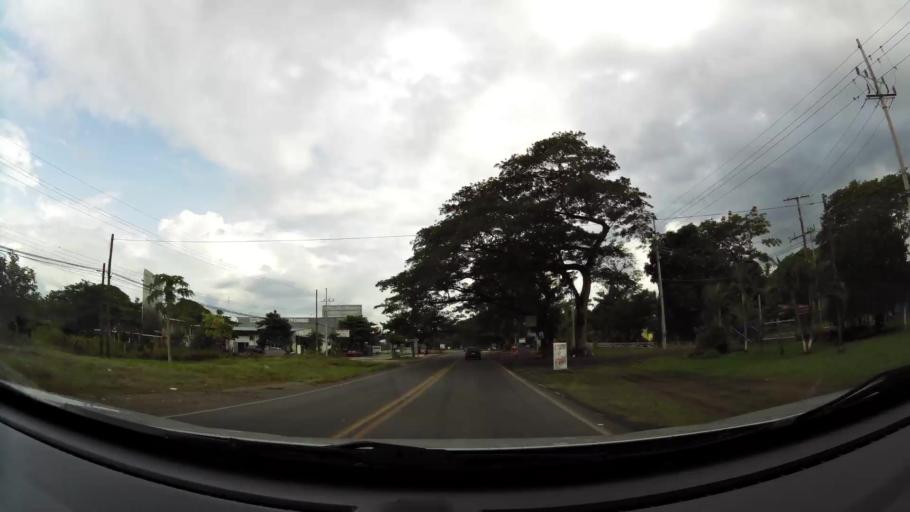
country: CR
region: Guanacaste
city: Juntas
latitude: 10.2592
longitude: -85.0163
